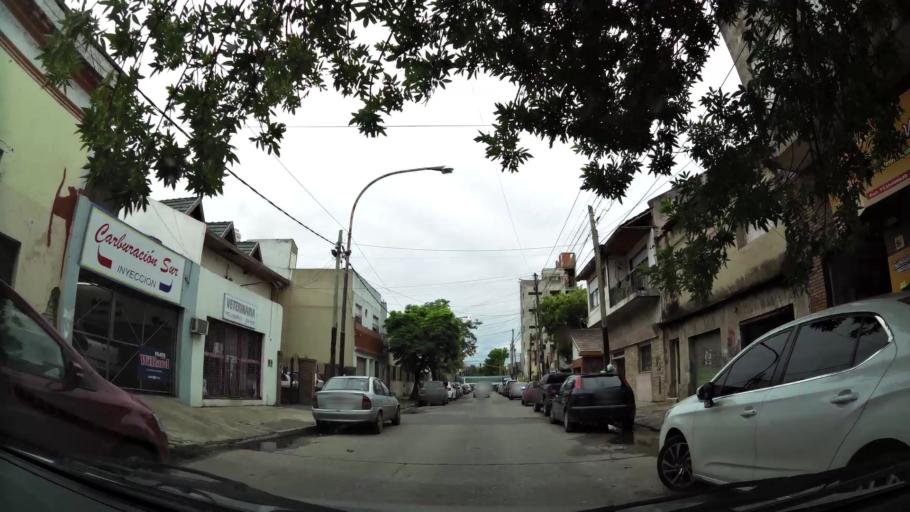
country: AR
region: Buenos Aires
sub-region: Partido de Lanus
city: Lanus
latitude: -34.7109
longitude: -58.3838
